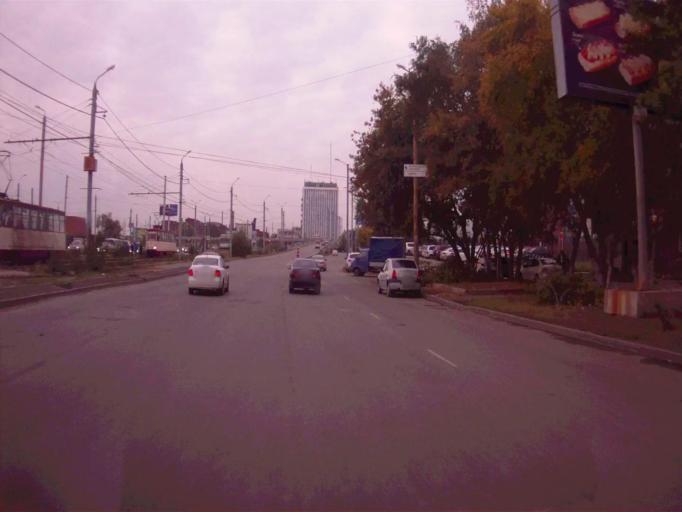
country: RU
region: Chelyabinsk
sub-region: Gorod Chelyabinsk
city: Chelyabinsk
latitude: 55.1405
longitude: 61.4120
